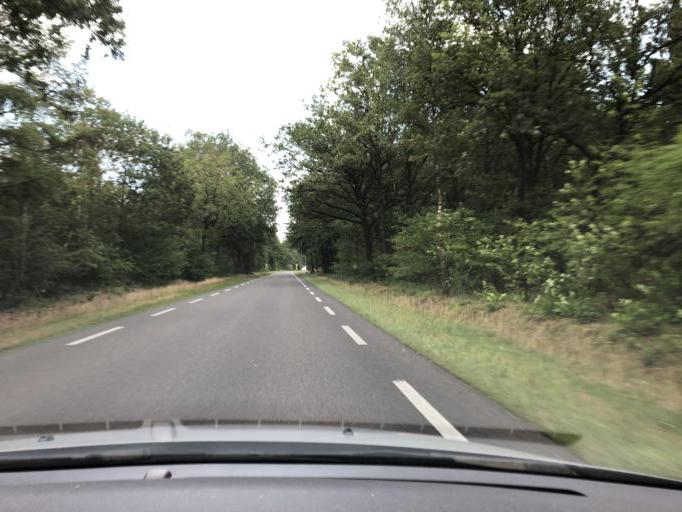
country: NL
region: Drenthe
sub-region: Gemeente Borger-Odoorn
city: Borger
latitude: 52.9385
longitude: 6.7343
